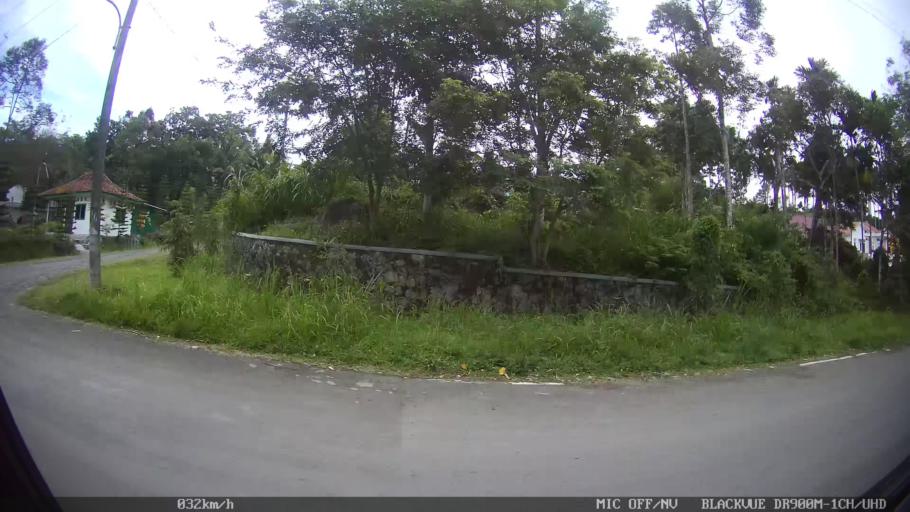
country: ID
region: Lampung
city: Bandarlampung
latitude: -5.4197
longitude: 105.1857
